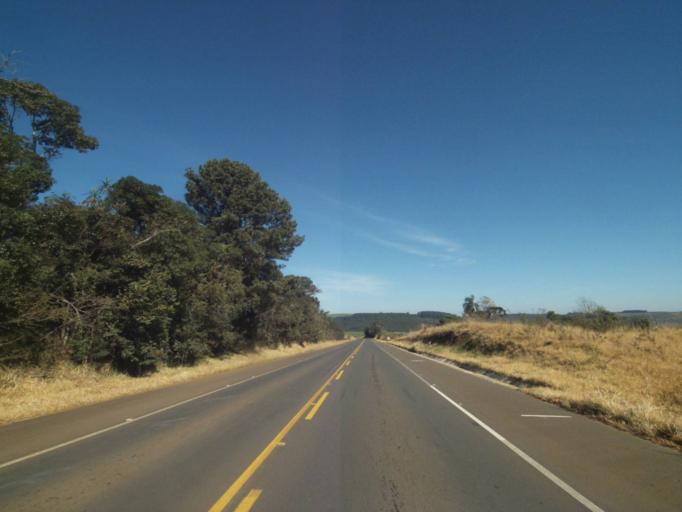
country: BR
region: Parana
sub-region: Tibagi
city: Tibagi
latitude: -24.7372
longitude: -50.4557
